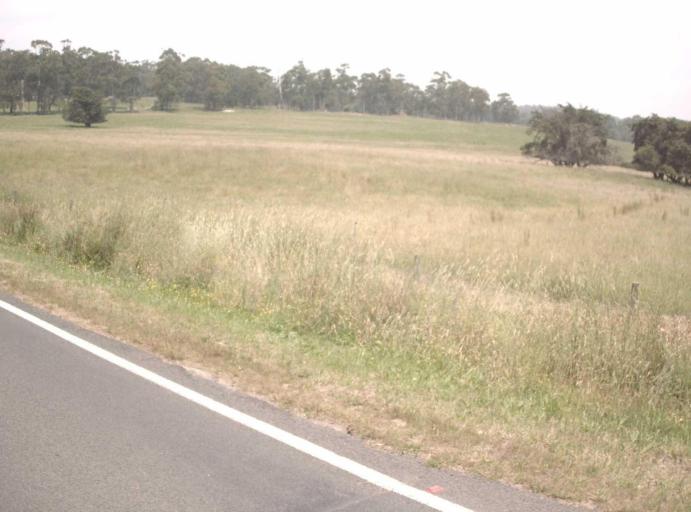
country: AU
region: Victoria
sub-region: Latrobe
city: Traralgon
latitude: -38.3742
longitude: 146.7543
